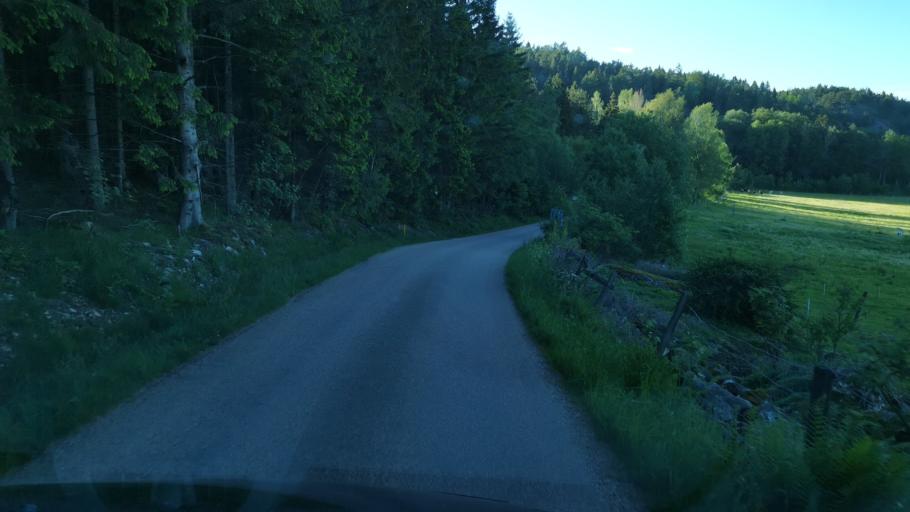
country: SE
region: Vaestra Goetaland
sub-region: Orust
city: Henan
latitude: 58.2727
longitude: 11.6385
